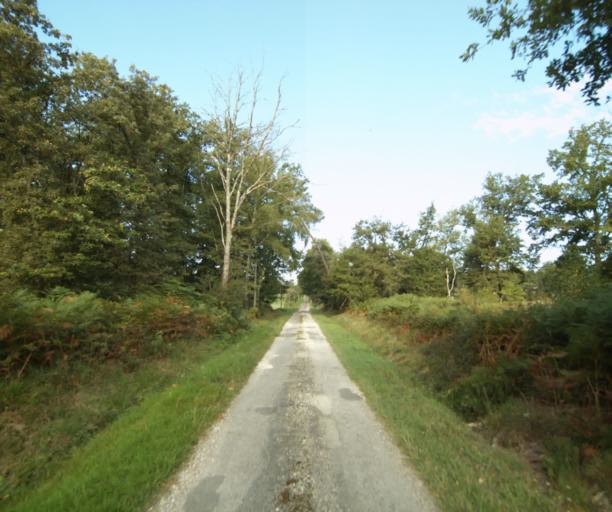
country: FR
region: Midi-Pyrenees
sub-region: Departement du Gers
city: Eauze
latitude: 43.8968
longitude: 0.0361
